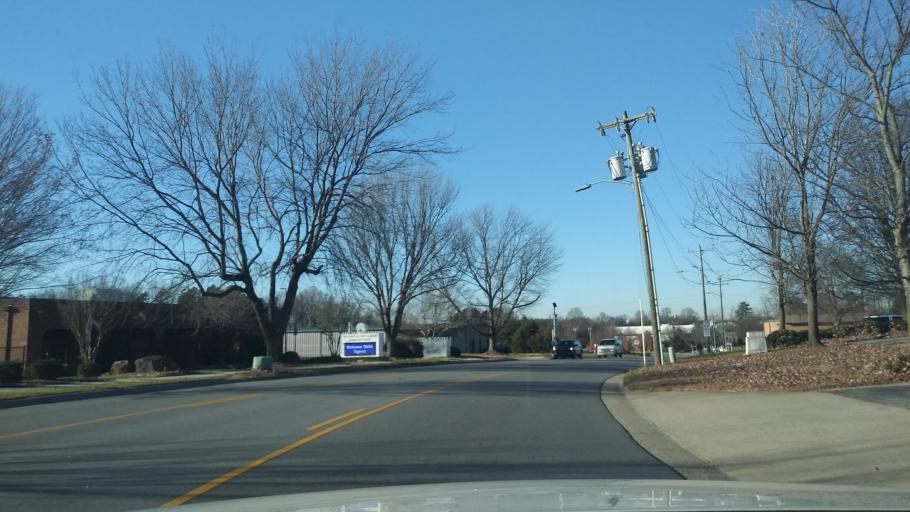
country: US
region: North Carolina
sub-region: Guilford County
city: Greensboro
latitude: 36.0266
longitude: -79.7767
